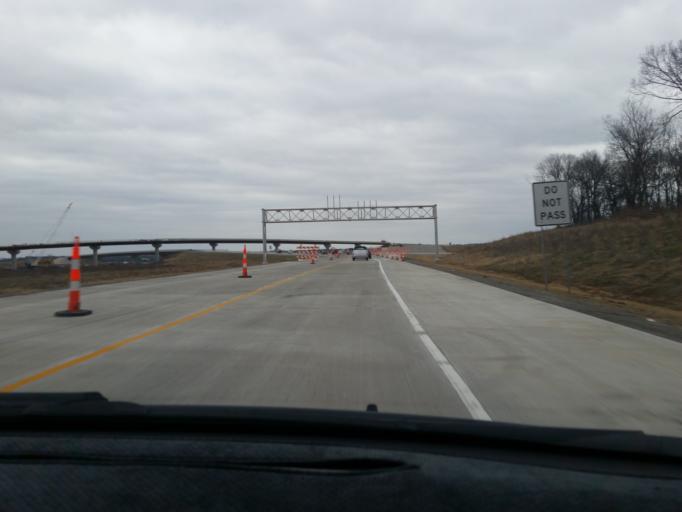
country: US
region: Kansas
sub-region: Douglas County
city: Lawrence
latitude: 38.9386
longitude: -95.1762
